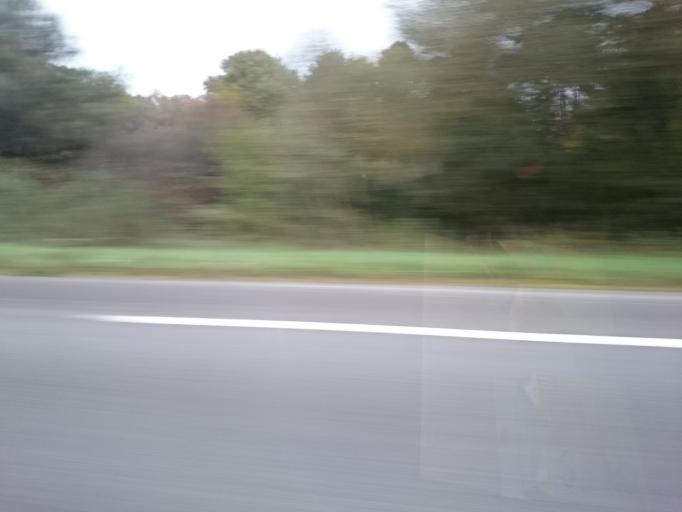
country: FR
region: Pays de la Loire
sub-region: Departement de la Loire-Atlantique
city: Orvault
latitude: 47.2922
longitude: -1.6122
